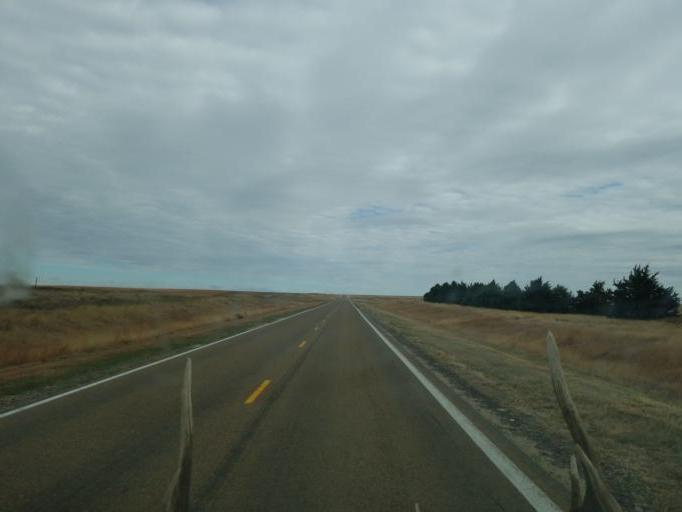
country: US
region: Kansas
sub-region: Wallace County
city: Sharon Springs
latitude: 39.0257
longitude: -101.3188
